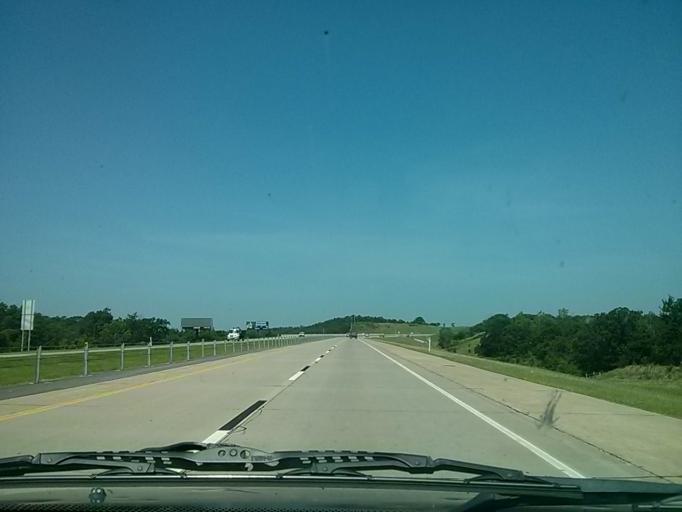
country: US
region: Oklahoma
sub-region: Tulsa County
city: Glenpool
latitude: 36.0090
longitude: -96.0329
